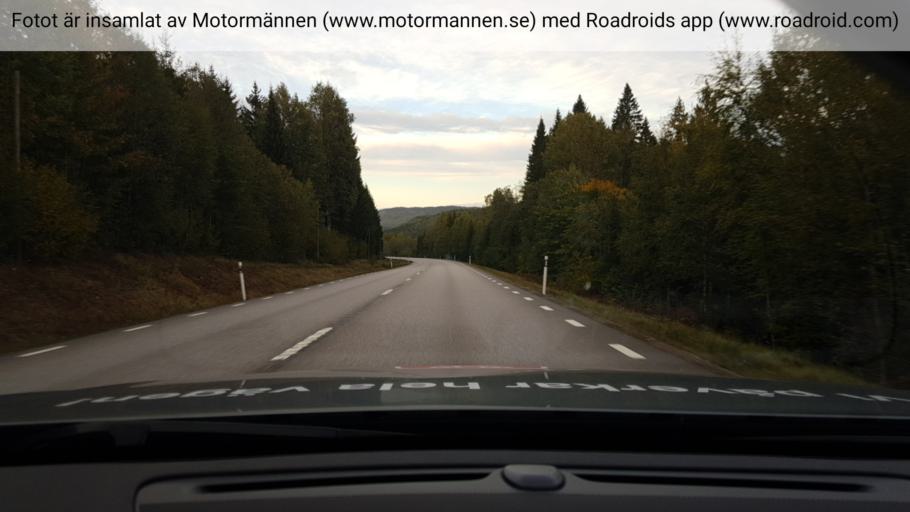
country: SE
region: Vaestra Goetaland
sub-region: Bengtsfors Kommun
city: Dals Langed
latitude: 59.0391
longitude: 12.4268
